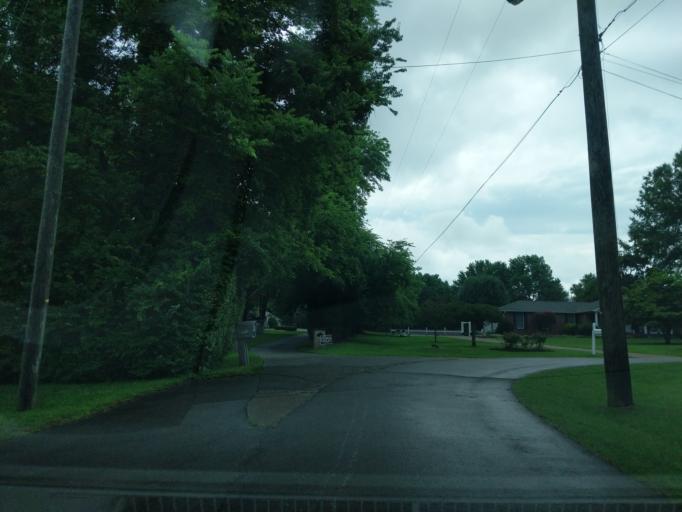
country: US
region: Tennessee
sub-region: Davidson County
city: Lakewood
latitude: 36.2313
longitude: -86.6936
